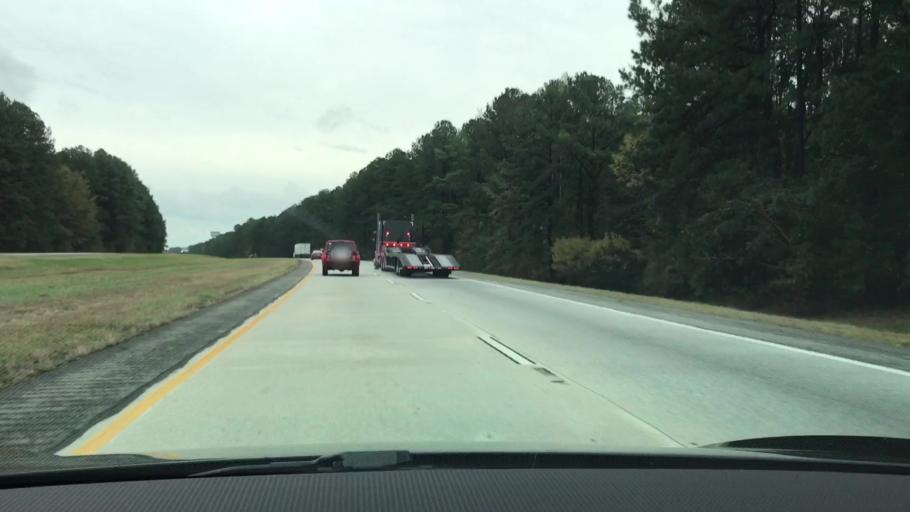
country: US
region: Georgia
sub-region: Taliaferro County
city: Crawfordville
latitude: 33.5322
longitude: -82.9873
